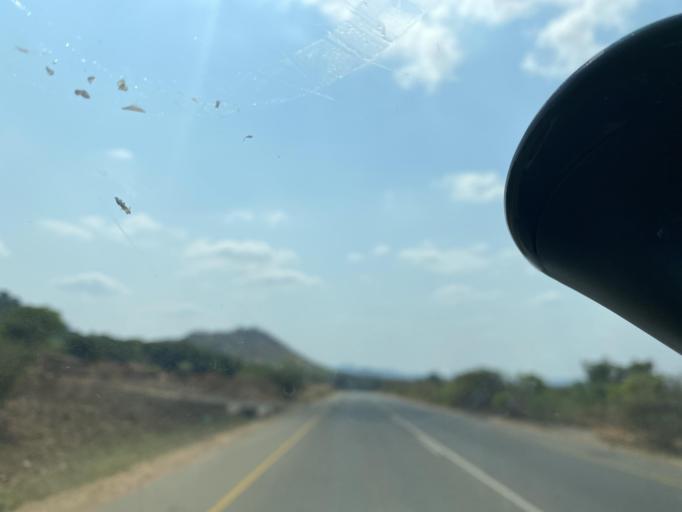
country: ZM
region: Lusaka
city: Chongwe
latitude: -15.5981
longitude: 28.7251
